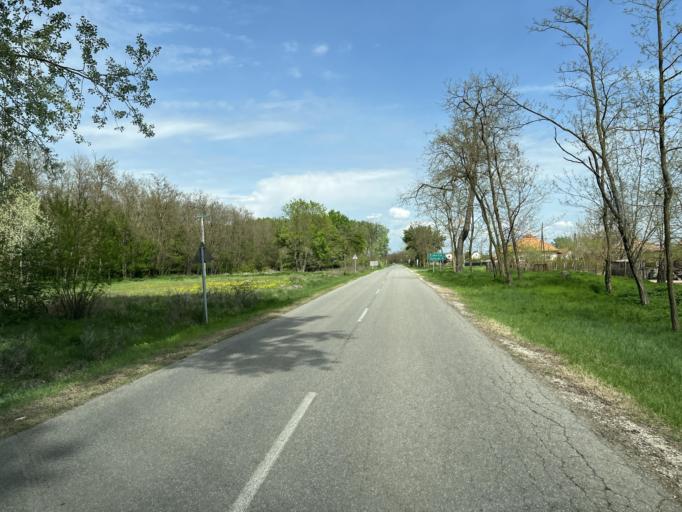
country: HU
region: Pest
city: Albertirsa
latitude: 47.1598
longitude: 19.6129
